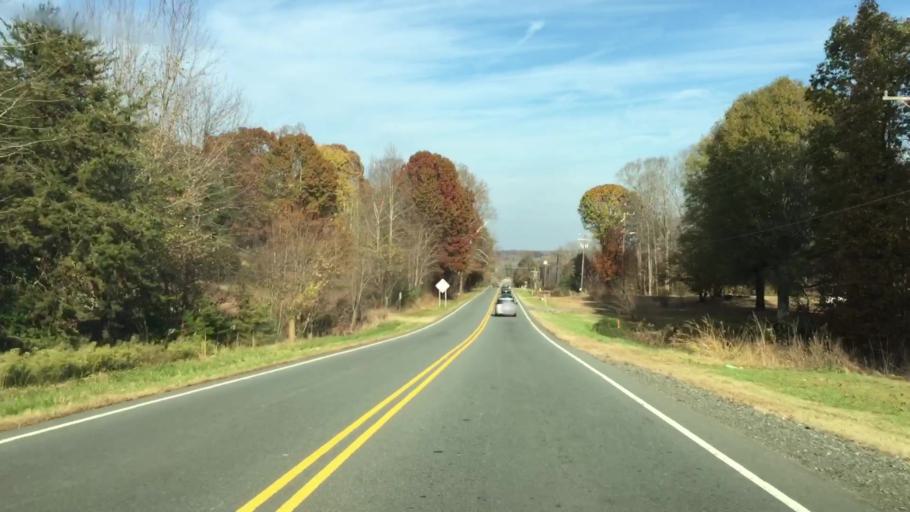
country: US
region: North Carolina
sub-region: Guilford County
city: Stokesdale
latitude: 36.2199
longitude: -80.0540
